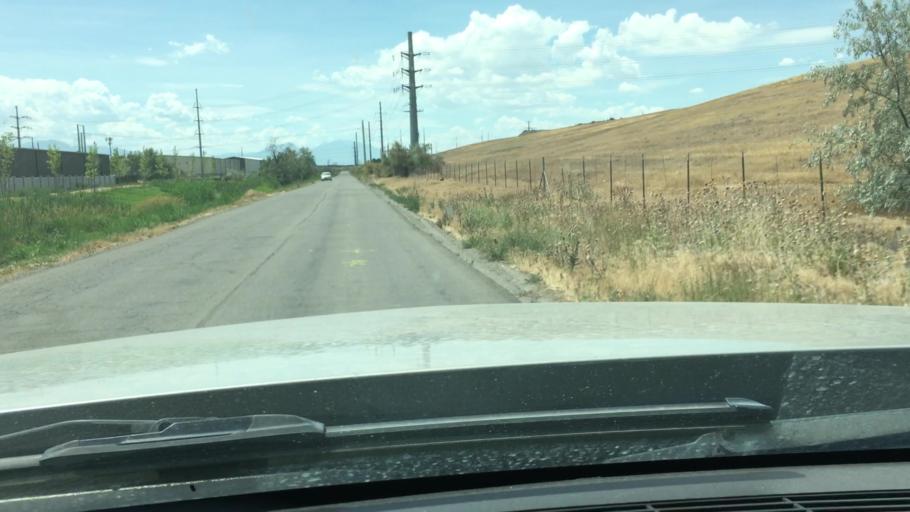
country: US
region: Utah
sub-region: Utah County
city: Pleasant Grove
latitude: 40.3393
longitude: -111.7599
